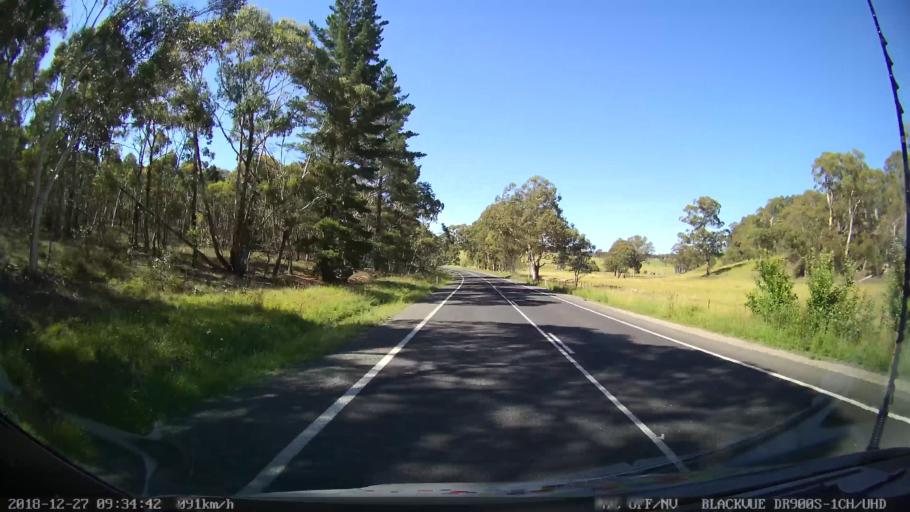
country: AU
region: New South Wales
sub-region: Lithgow
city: Portland
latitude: -33.2296
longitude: 150.0267
